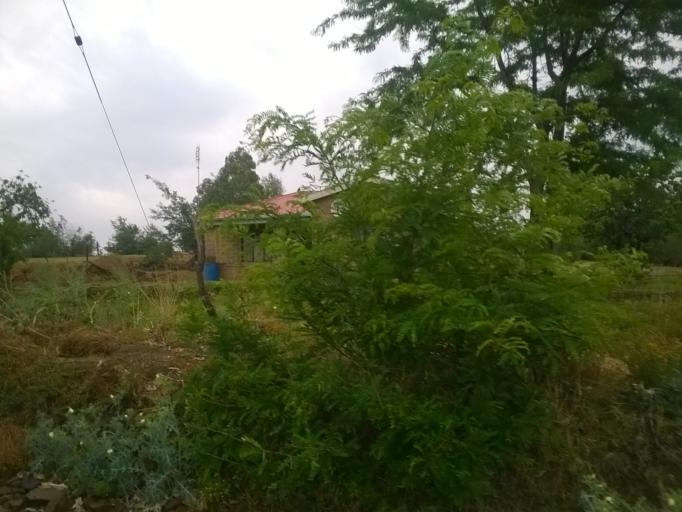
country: LS
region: Berea
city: Teyateyaneng
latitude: -29.1382
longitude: 27.7375
